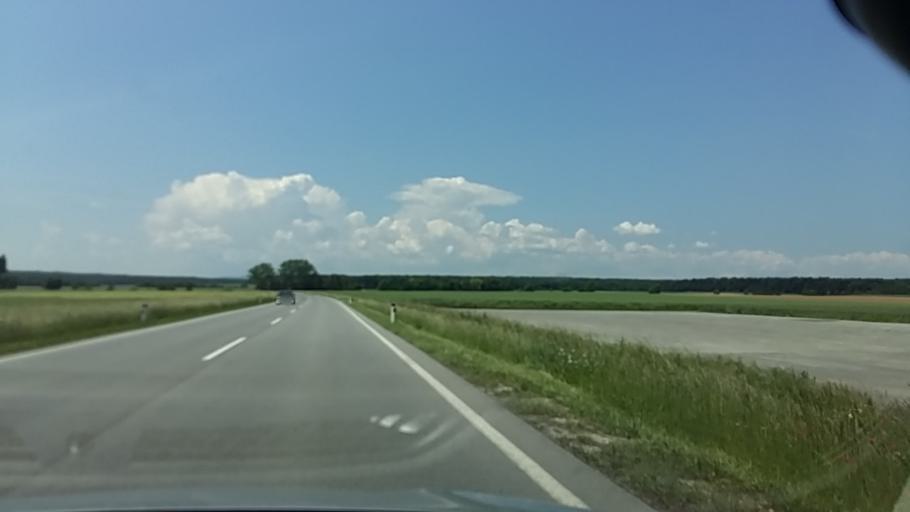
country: AT
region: Burgenland
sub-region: Politischer Bezirk Oberpullendorf
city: Raiding
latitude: 47.5366
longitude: 16.5453
